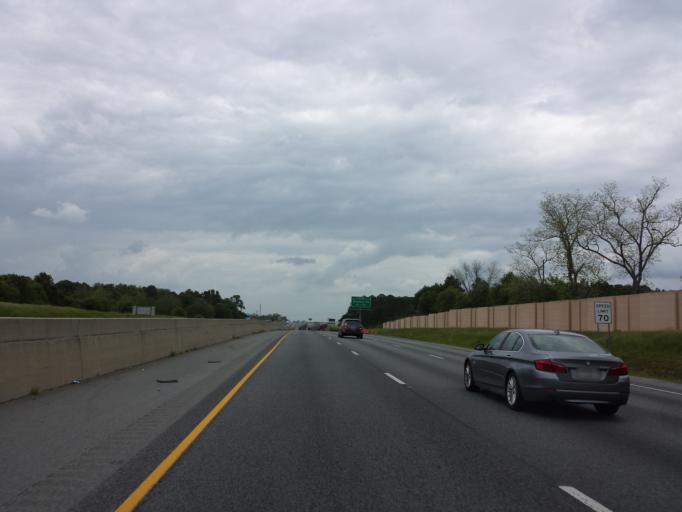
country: US
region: Georgia
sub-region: Tift County
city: Tifton
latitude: 31.4883
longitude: -83.5156
